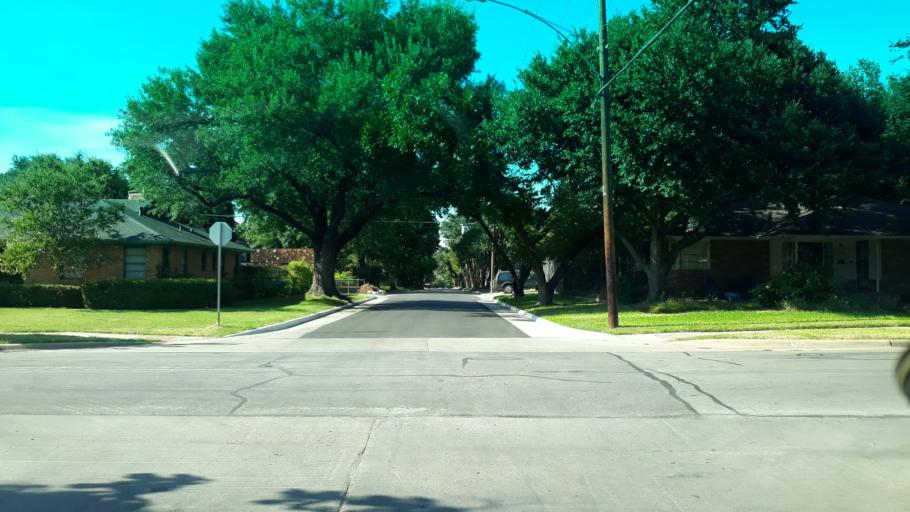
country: US
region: Texas
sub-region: Dallas County
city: Highland Park
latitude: 32.8265
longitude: -96.7560
